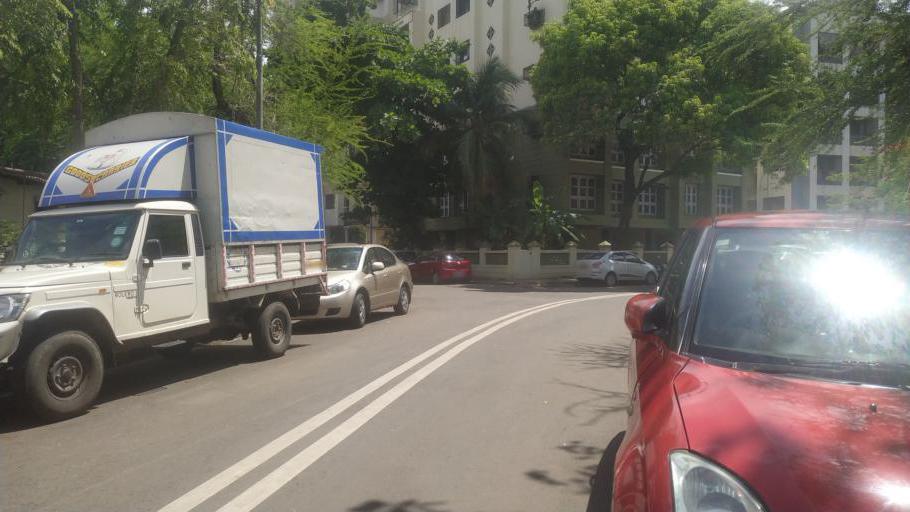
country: IN
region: Maharashtra
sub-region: Mumbai Suburban
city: Mumbai
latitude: 19.0614
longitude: 72.8812
